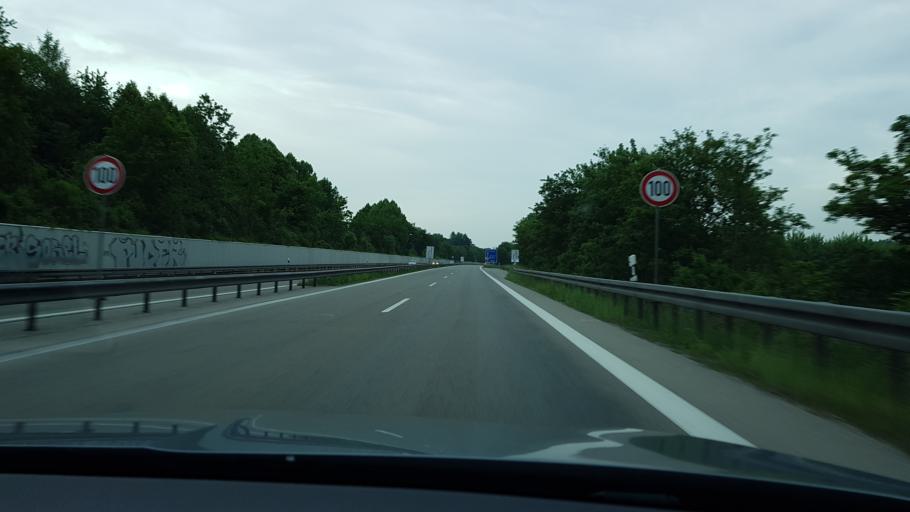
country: DE
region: Bavaria
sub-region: Upper Bavaria
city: Schaftlarn
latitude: 48.0086
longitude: 11.4027
